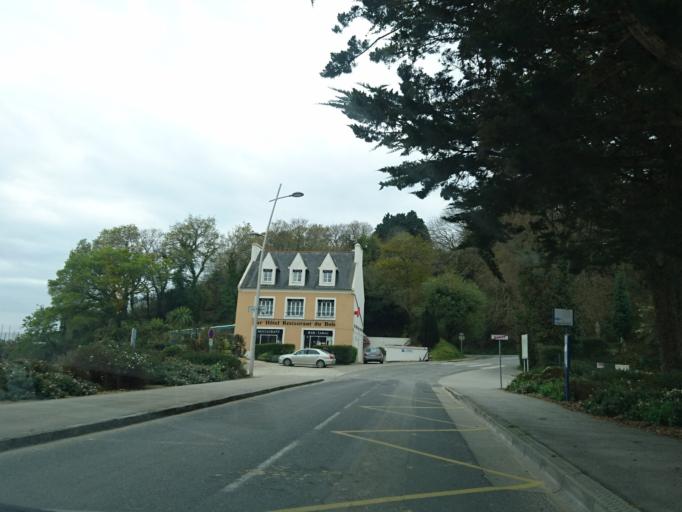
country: FR
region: Brittany
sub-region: Departement du Finistere
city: Roscanvel
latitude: 48.3617
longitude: -4.5545
